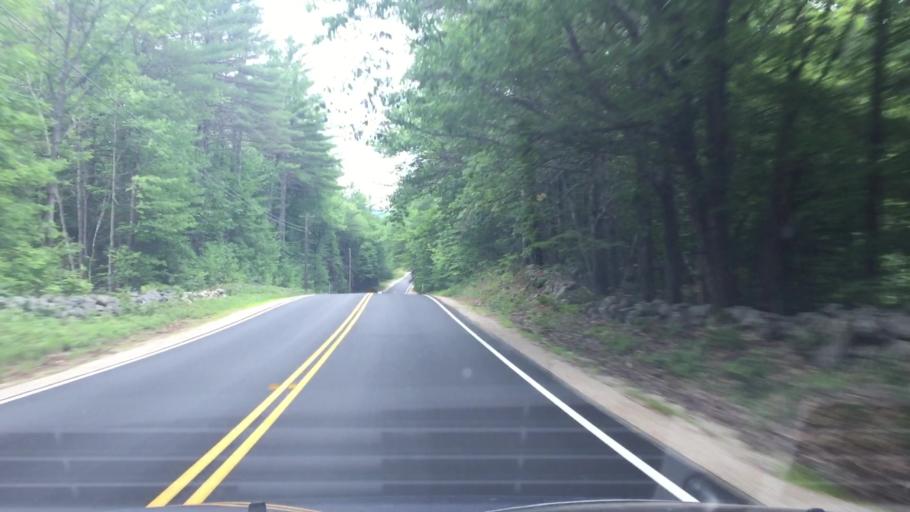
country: US
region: New Hampshire
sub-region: Carroll County
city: Freedom
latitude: 43.8340
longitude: -71.0777
